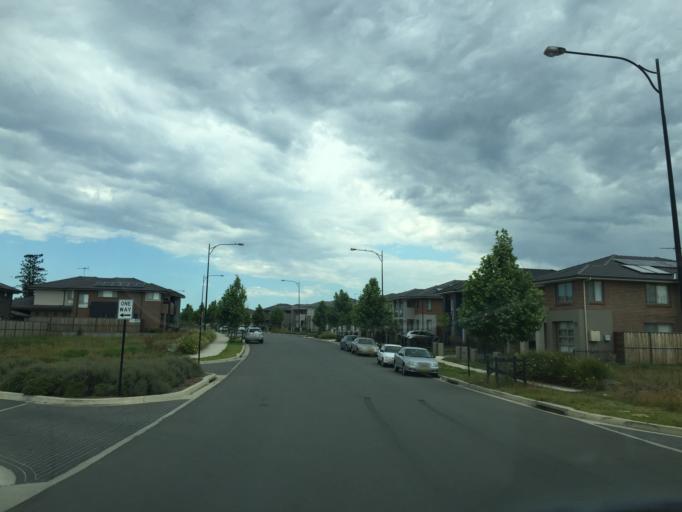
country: AU
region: New South Wales
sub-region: Blacktown
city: Doonside
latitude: -33.7765
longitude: 150.8688
